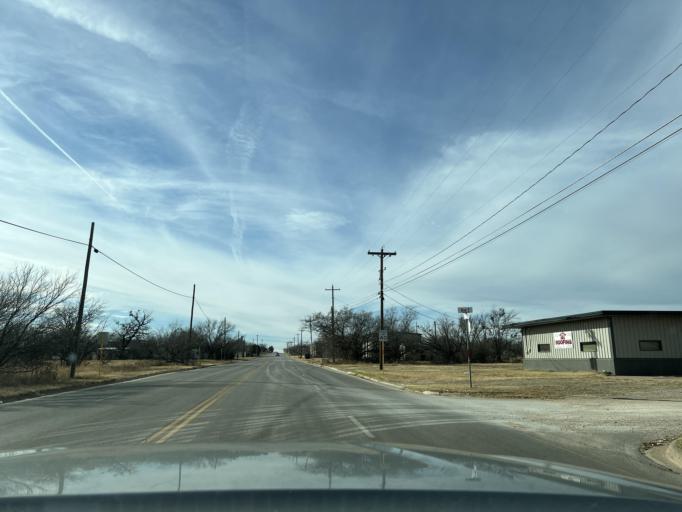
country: US
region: Texas
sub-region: Jones County
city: Anson
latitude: 32.7515
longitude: -99.8894
